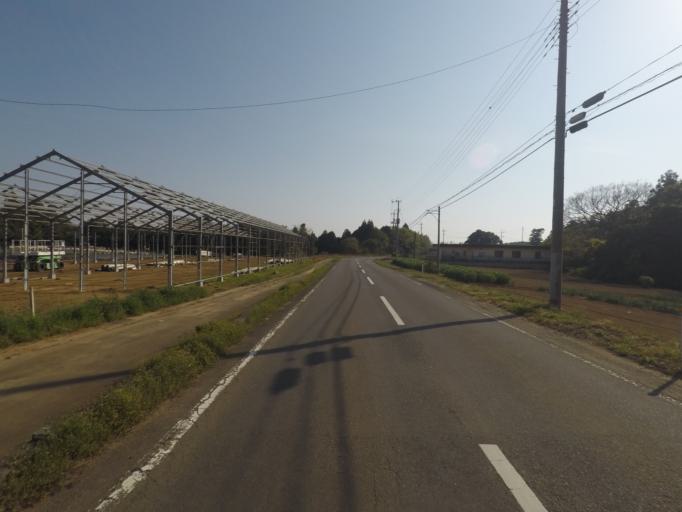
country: JP
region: Ibaraki
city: Inashiki
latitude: 36.0672
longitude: 140.4480
